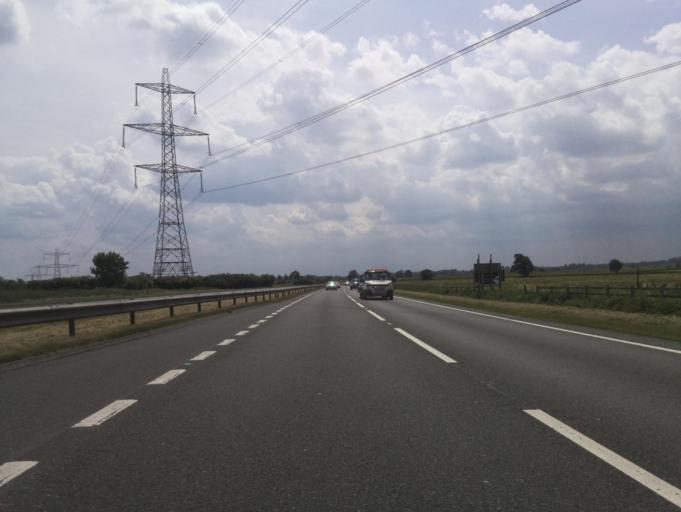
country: GB
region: England
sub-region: North Yorkshire
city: Thirsk
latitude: 54.2756
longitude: -1.3417
